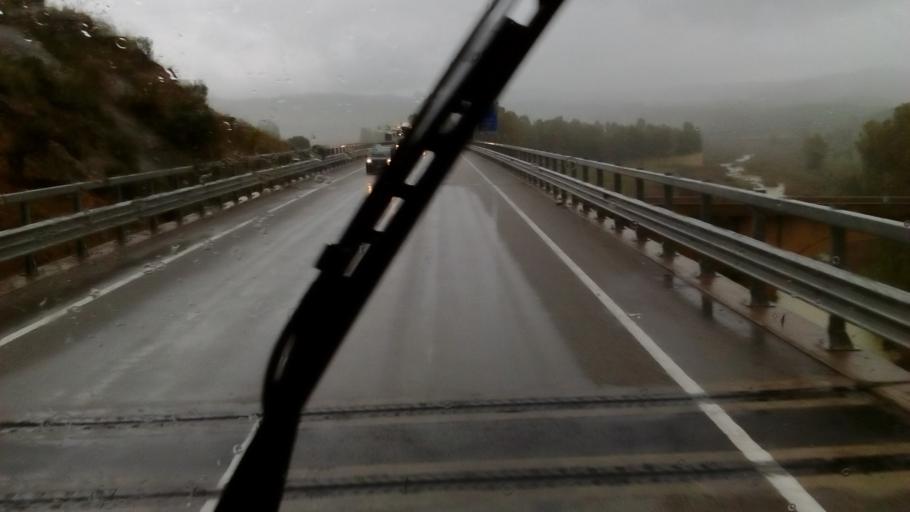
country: IT
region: Sicily
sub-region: Enna
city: Pietraperzia
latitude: 37.4964
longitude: 14.1448
